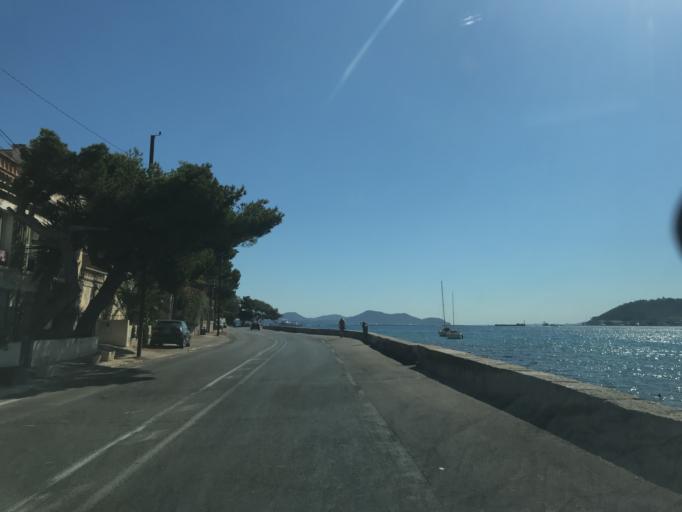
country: FR
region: Provence-Alpes-Cote d'Azur
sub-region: Departement du Var
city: La Seyne-sur-Mer
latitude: 43.0930
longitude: 5.9071
